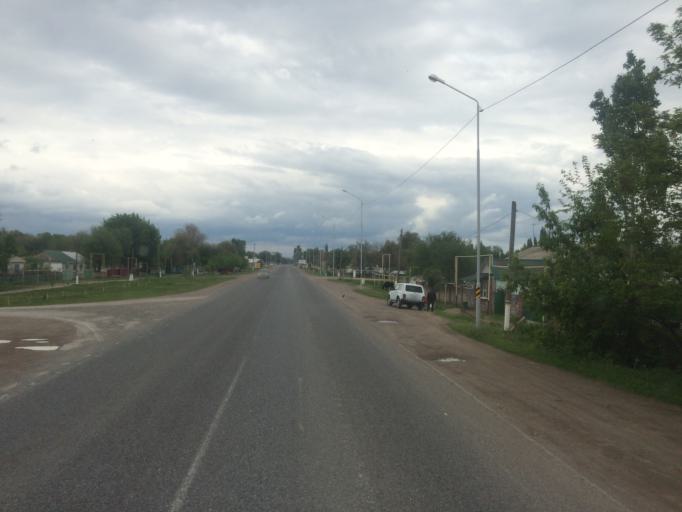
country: KZ
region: Zhambyl
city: Georgiyevka
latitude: 43.2279
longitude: 74.3878
